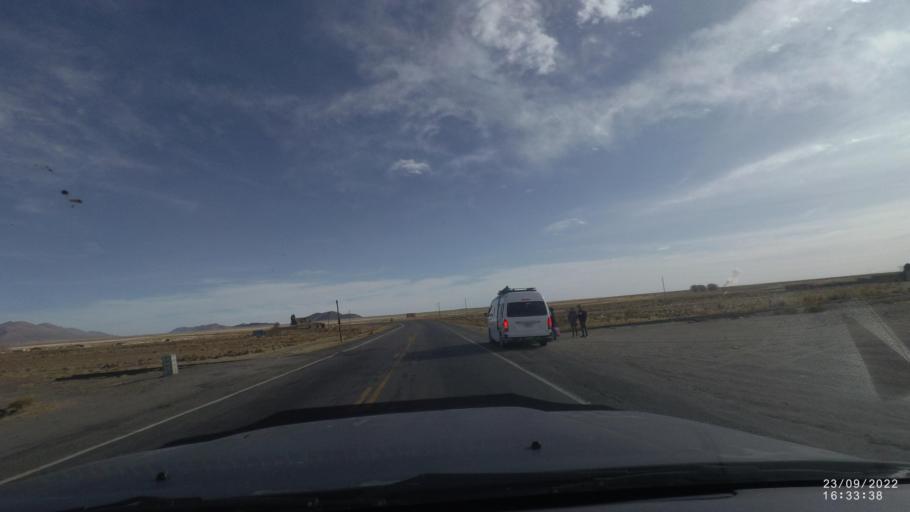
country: BO
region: Oruro
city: Machacamarca
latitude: -18.1771
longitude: -67.0153
